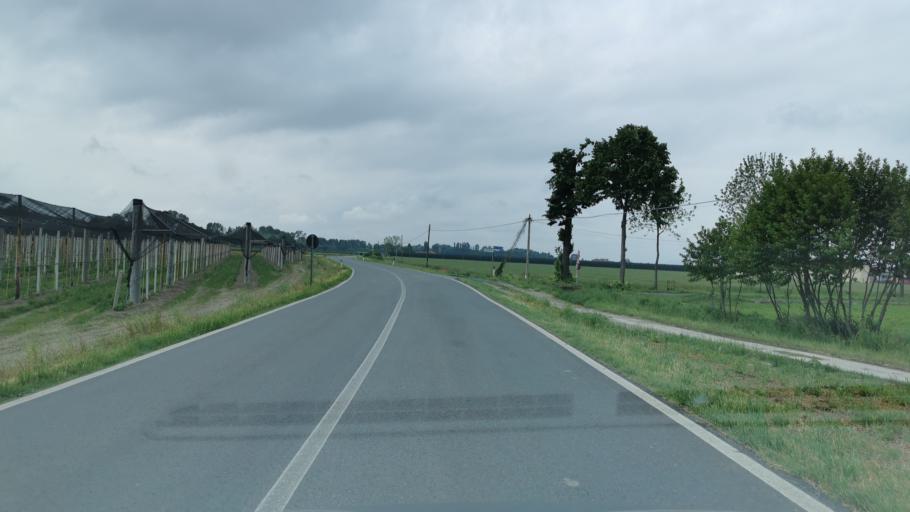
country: IT
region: Piedmont
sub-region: Provincia di Cuneo
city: Savigliano
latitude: 44.6219
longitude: 7.6322
